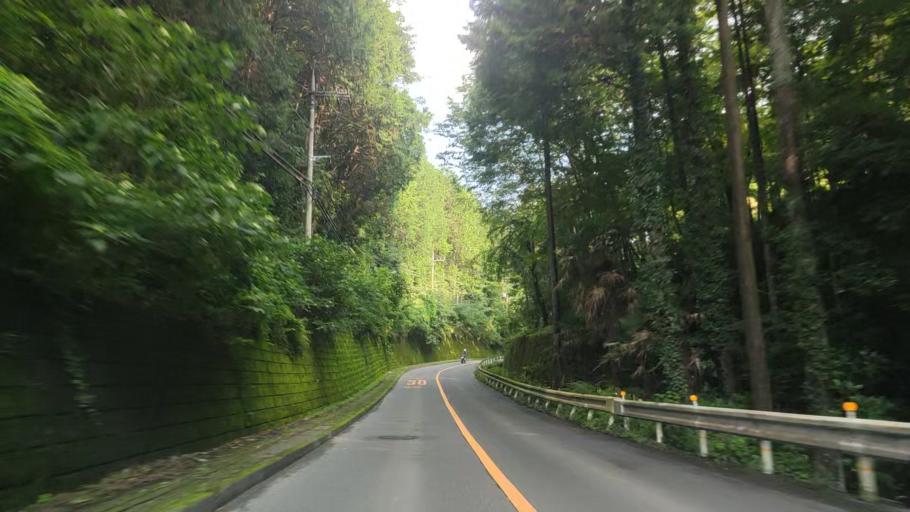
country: JP
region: Saitama
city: Hanno
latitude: 35.8299
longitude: 139.2706
